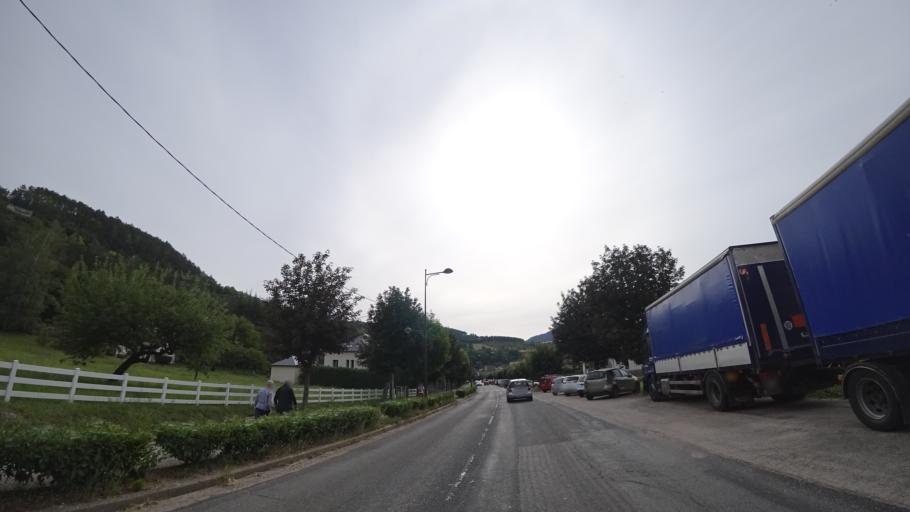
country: FR
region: Languedoc-Roussillon
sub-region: Departement de la Lozere
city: La Canourgue
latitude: 44.4334
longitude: 3.2097
